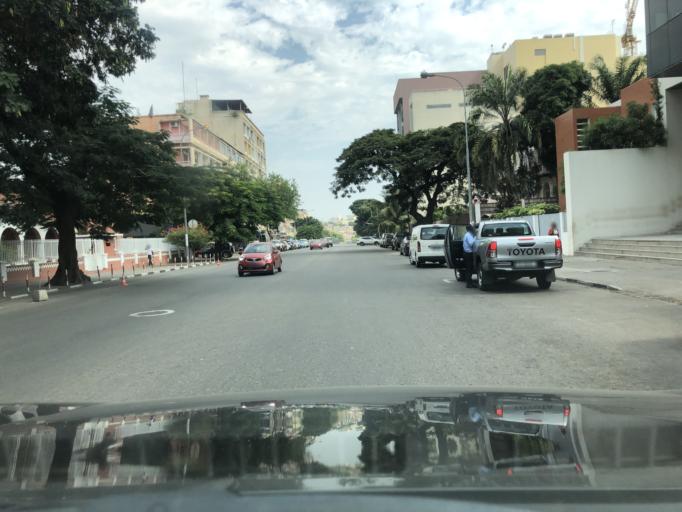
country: AO
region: Luanda
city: Luanda
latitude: -8.8243
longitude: 13.2284
